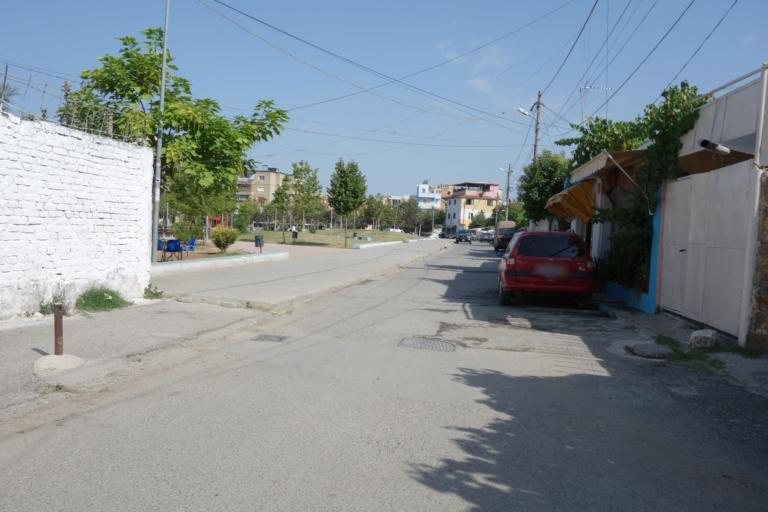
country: AL
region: Tirane
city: Tirana
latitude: 41.3270
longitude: 19.8374
